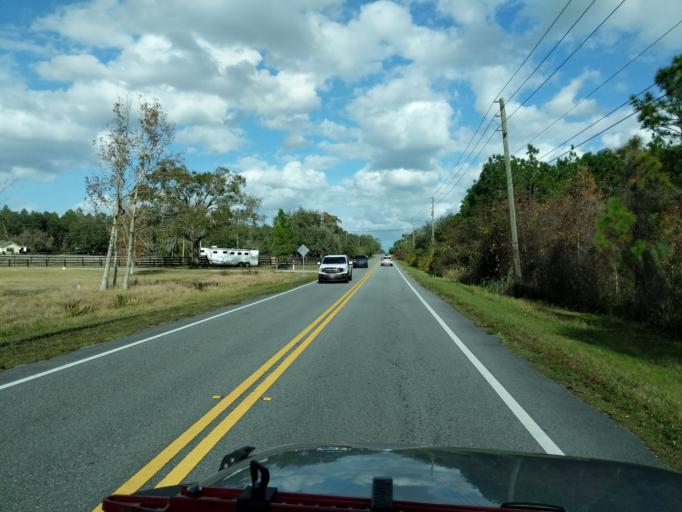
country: US
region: Florida
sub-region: Seminole County
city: Geneva
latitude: 28.6974
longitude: -81.1381
